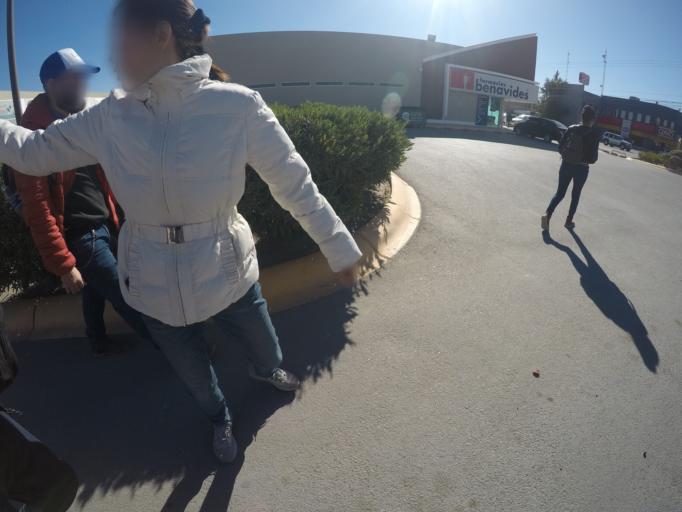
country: US
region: Texas
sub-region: El Paso County
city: Socorro
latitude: 31.6945
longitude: -106.3744
